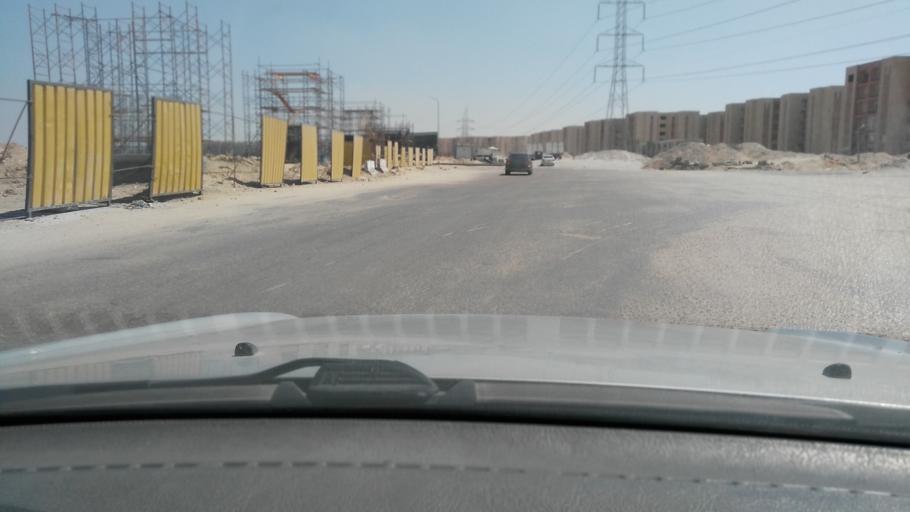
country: EG
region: Al Jizah
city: Madinat Sittah Uktubar
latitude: 29.9114
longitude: 30.9323
